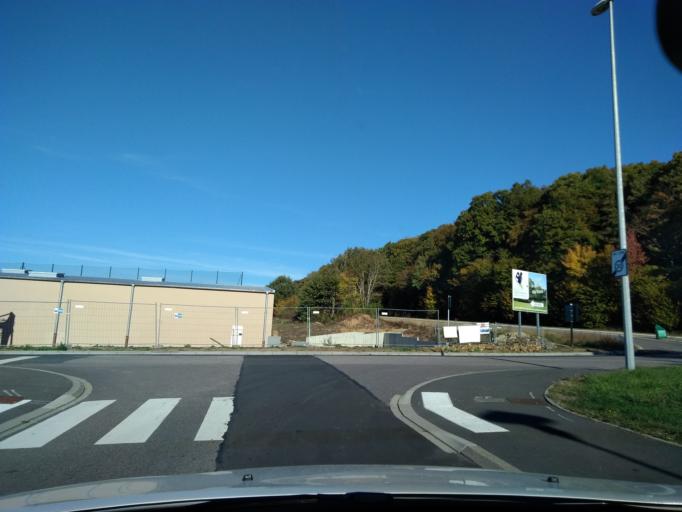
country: FR
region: Lorraine
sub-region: Departement de la Moselle
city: Rouhling
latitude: 49.1234
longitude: 7.0261
